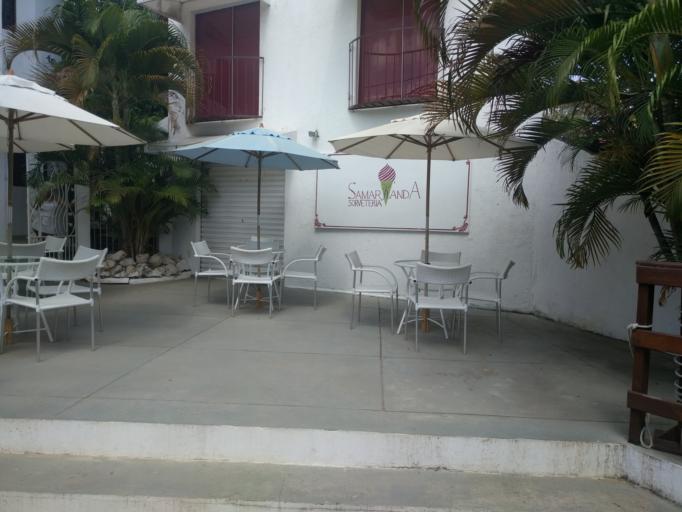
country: BR
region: Rio Grande do Norte
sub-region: Ares
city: Ares
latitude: -6.2312
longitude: -35.0459
